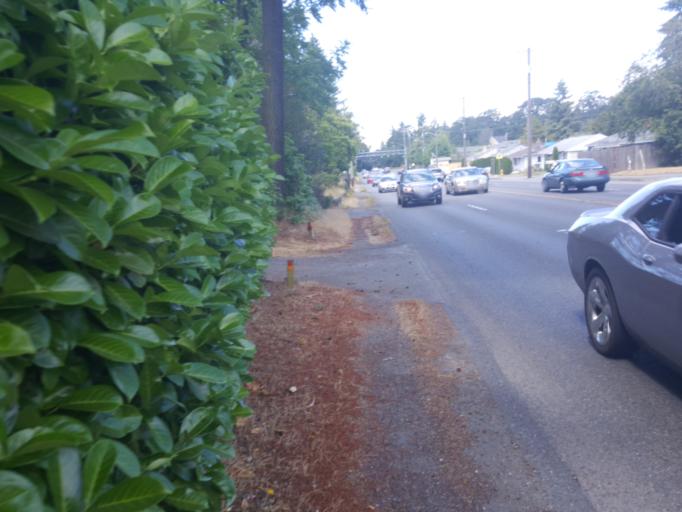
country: US
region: Washington
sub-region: Pierce County
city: Lakewood
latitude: 47.1816
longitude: -122.5257
